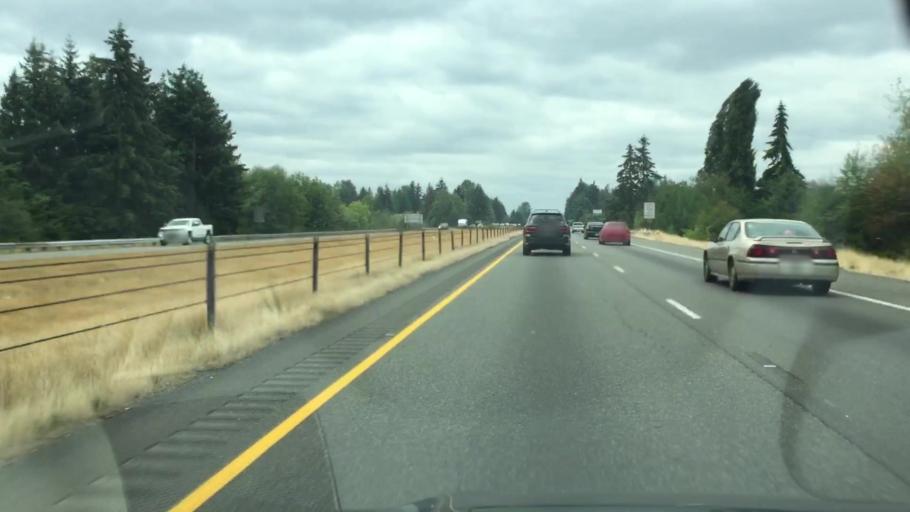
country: US
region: Washington
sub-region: Pierce County
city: Summit
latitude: 47.1582
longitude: -122.3334
